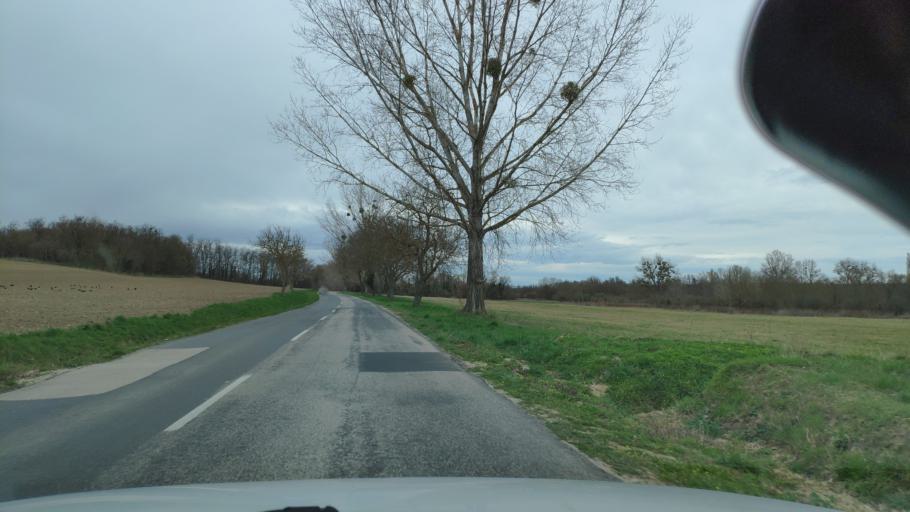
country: HU
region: Zala
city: Sarmellek
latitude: 46.6659
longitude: 17.1132
